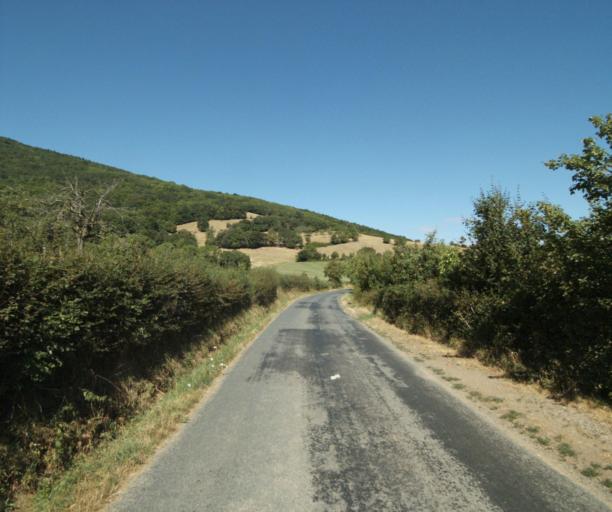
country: FR
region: Rhone-Alpes
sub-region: Departement du Rhone
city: Saint-Romain-de-Popey
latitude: 45.8244
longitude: 4.5327
